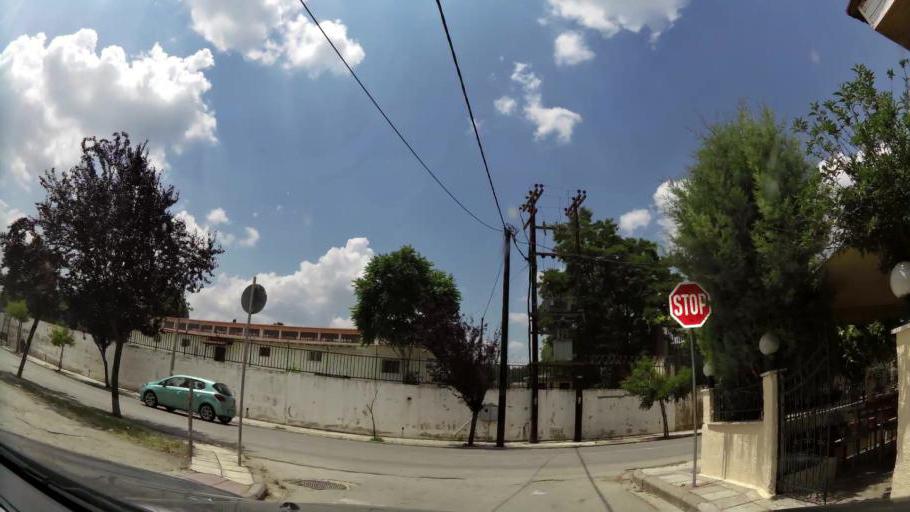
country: GR
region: West Macedonia
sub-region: Nomos Kozanis
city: Kozani
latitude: 40.2924
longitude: 21.7829
